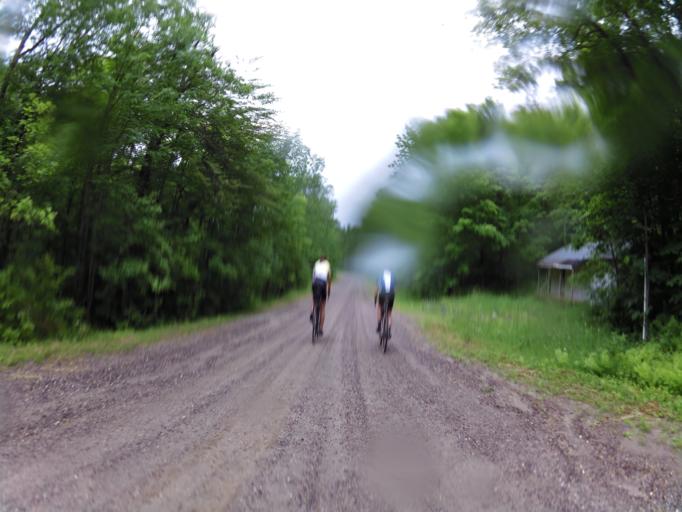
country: CA
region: Ontario
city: Renfrew
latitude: 45.1025
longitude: -76.6040
